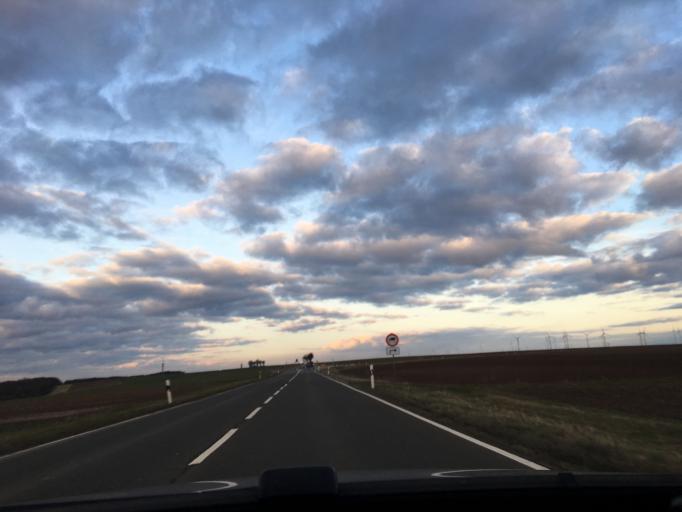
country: DE
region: Rheinland-Pfalz
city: Freimersheim
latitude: 49.7224
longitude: 8.0892
